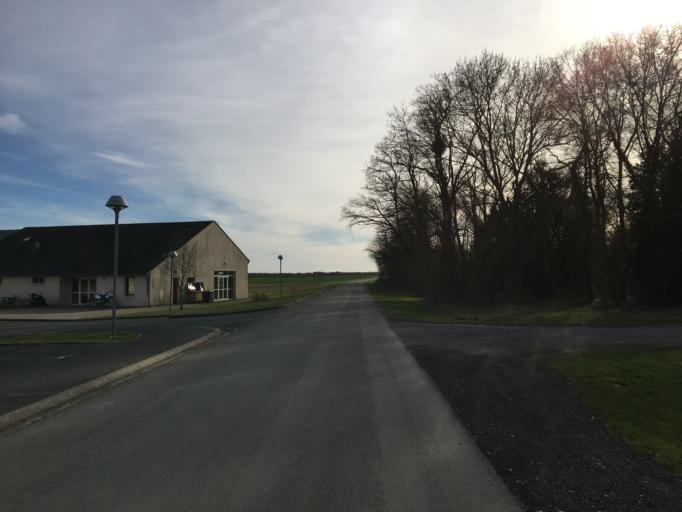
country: FR
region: Centre
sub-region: Departement du Loiret
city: Epieds-en-Beauce
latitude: 47.8891
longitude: 1.6270
